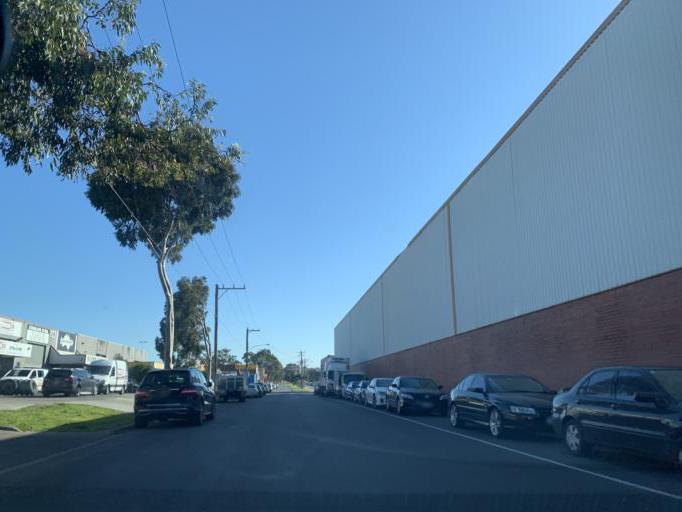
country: AU
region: Victoria
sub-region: Greater Dandenong
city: Dandenong
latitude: -37.9904
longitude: 145.1965
